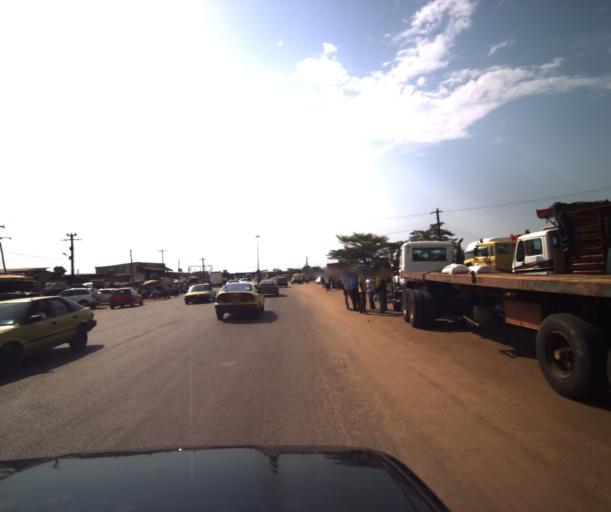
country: CM
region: Littoral
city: Douala
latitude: 4.0187
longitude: 9.7239
